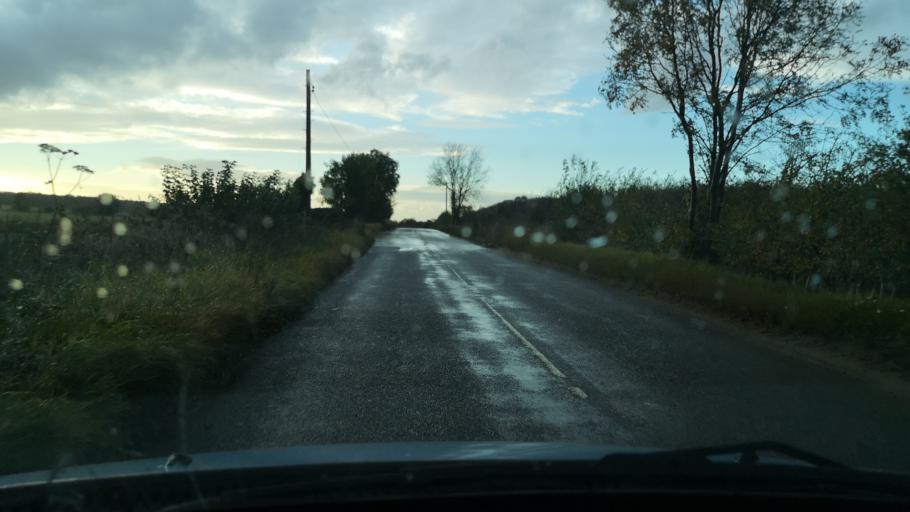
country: GB
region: England
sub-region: City and Borough of Wakefield
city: Darrington
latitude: 53.6463
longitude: -1.2480
